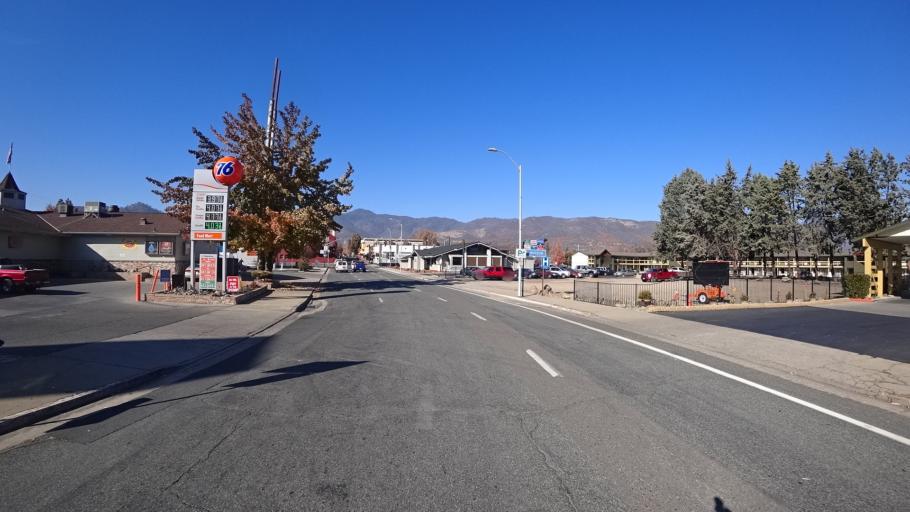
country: US
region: California
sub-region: Siskiyou County
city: Yreka
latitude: 41.7312
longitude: -122.6344
